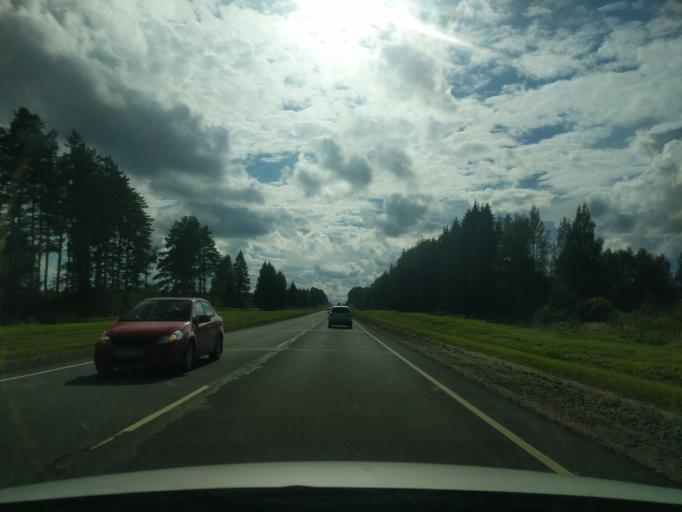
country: RU
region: Jaroslavl
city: Nekrasovskoye
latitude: 57.6235
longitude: 40.3622
